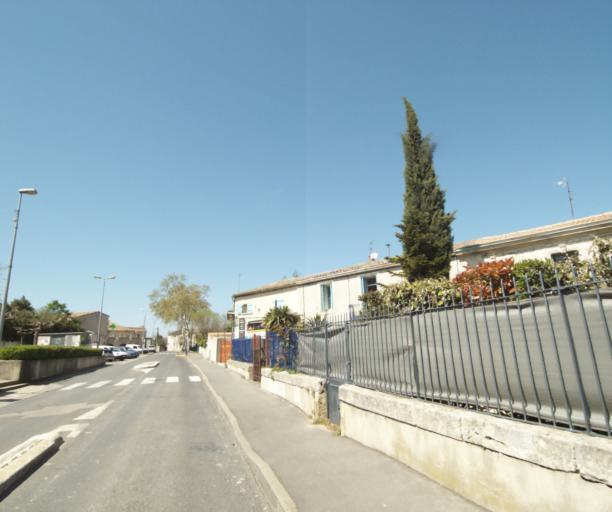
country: FR
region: Languedoc-Roussillon
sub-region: Departement de l'Herault
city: Sussargues
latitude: 43.7120
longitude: 4.0057
